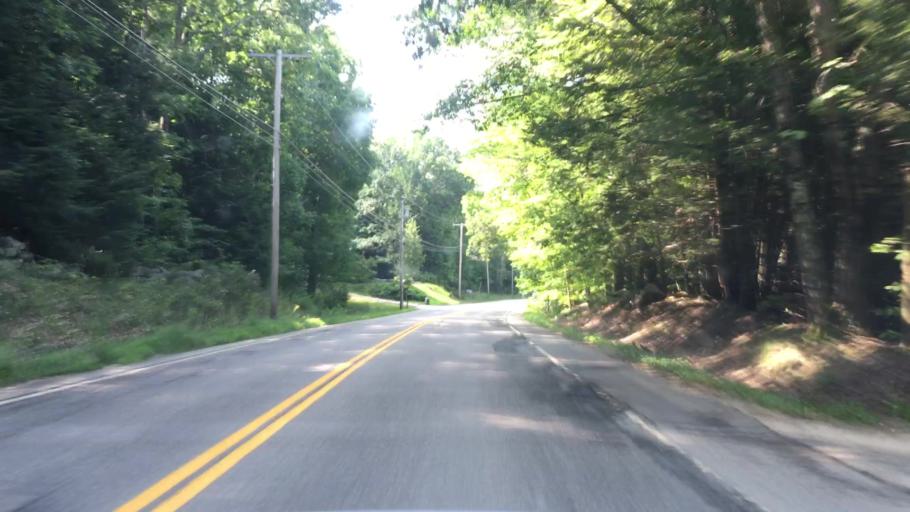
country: US
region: Maine
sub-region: Cumberland County
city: Raymond
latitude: 43.9092
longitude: -70.4404
